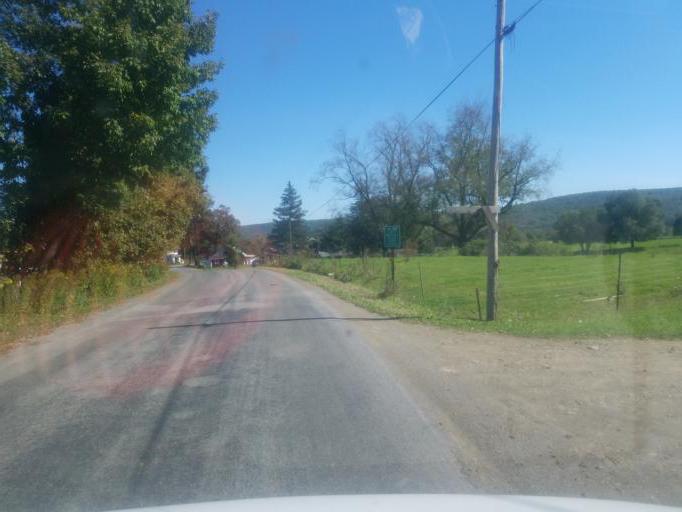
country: US
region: New York
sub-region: Allegany County
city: Friendship
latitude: 42.3006
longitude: -78.1922
